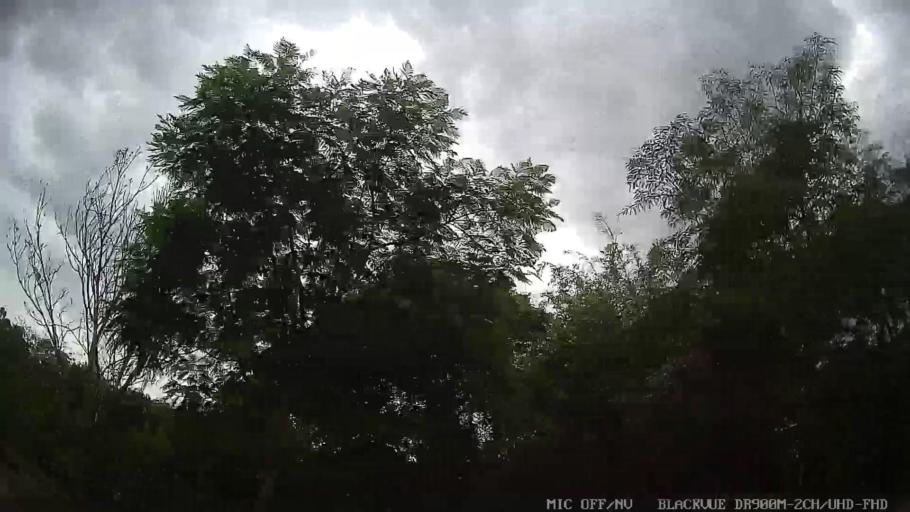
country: BR
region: Sao Paulo
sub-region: Itatiba
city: Itatiba
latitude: -23.0052
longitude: -46.8613
